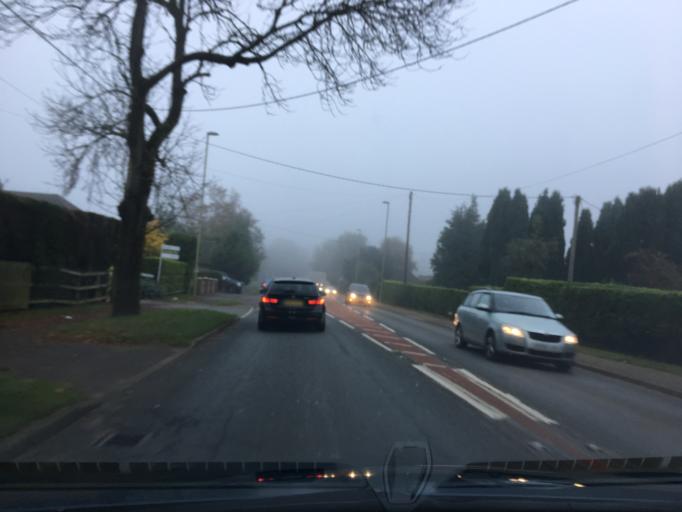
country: GB
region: England
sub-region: Hampshire
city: Four Marks
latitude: 51.1101
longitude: -1.0481
